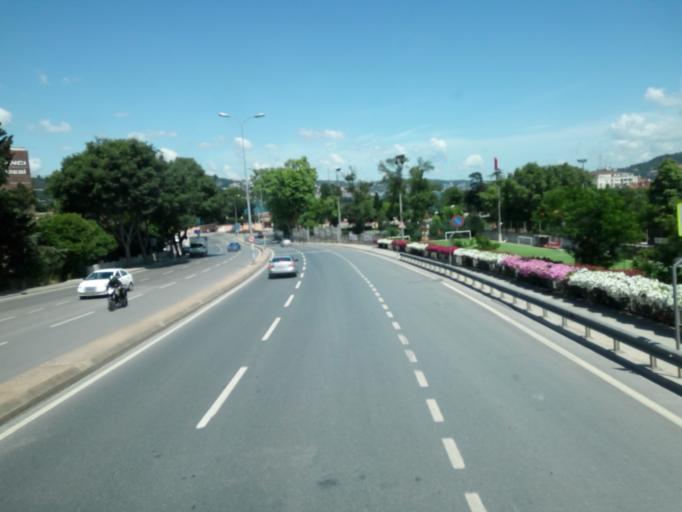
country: TR
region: Istanbul
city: UEskuedar
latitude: 41.0412
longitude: 29.0423
